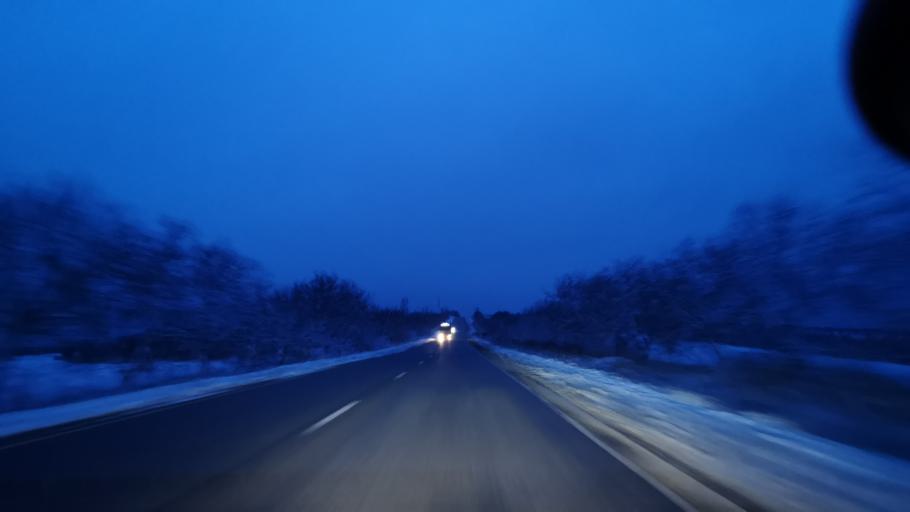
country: MD
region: Orhei
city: Orhei
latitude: 47.5436
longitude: 28.7928
